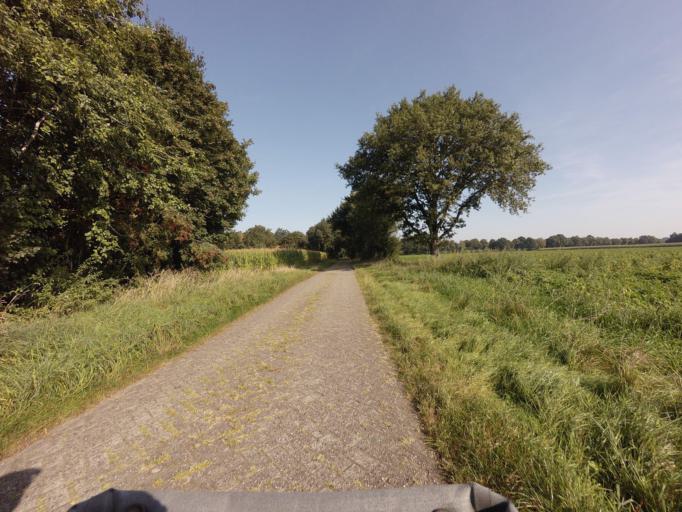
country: DE
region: Lower Saxony
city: Laar
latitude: 52.5934
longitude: 6.7792
